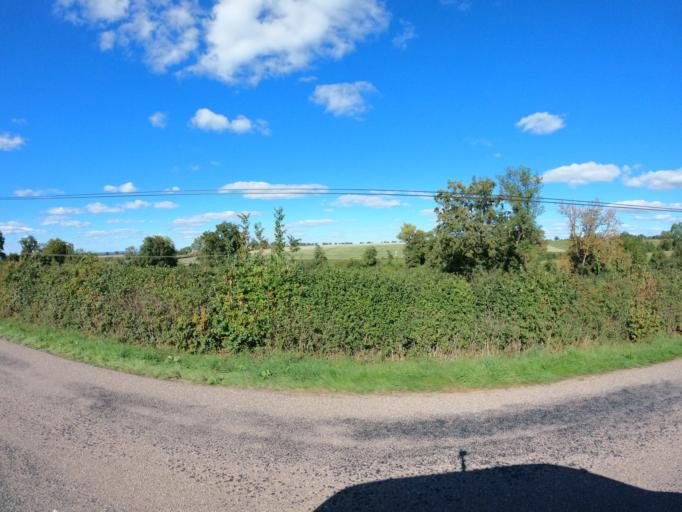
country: FR
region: Auvergne
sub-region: Departement de l'Allier
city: Buxieres-les-Mines
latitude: 46.4025
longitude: 2.9468
